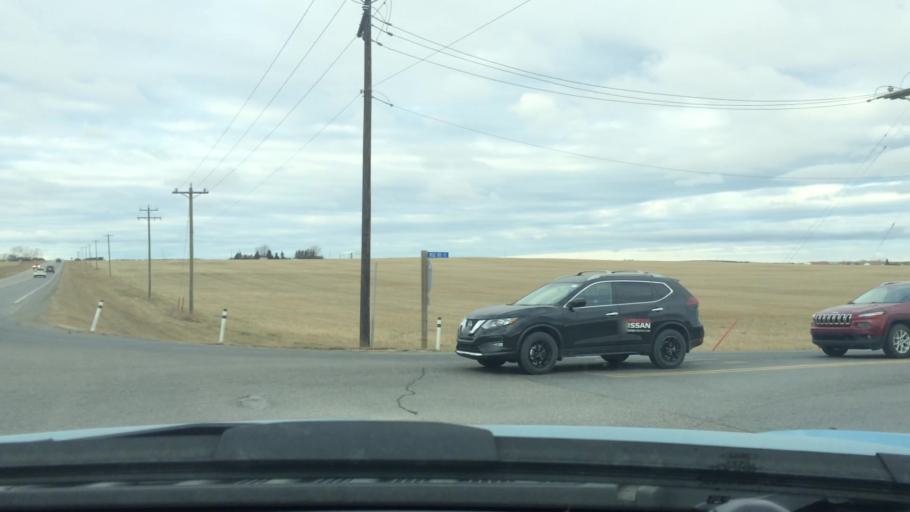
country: CA
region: Alberta
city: Airdrie
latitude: 51.2126
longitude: -114.0247
